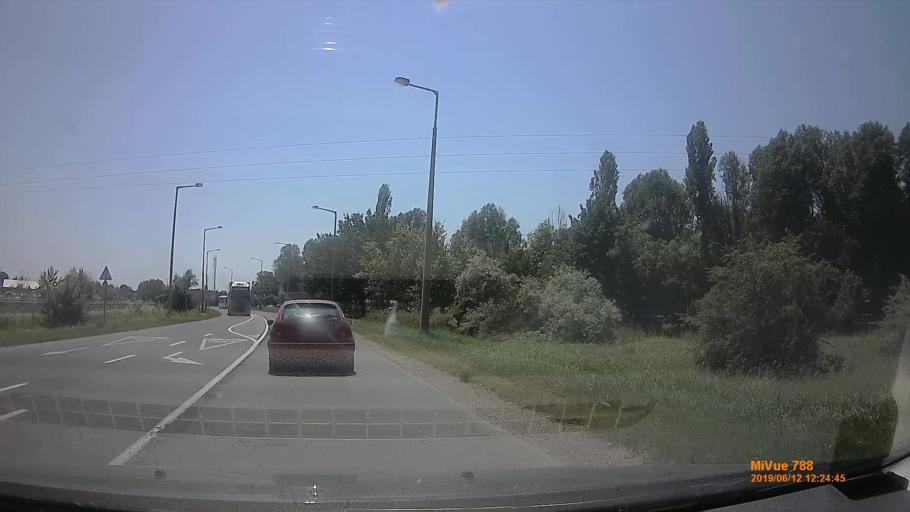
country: HU
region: Bacs-Kiskun
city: Kecskemet
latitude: 46.8867
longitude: 19.7036
